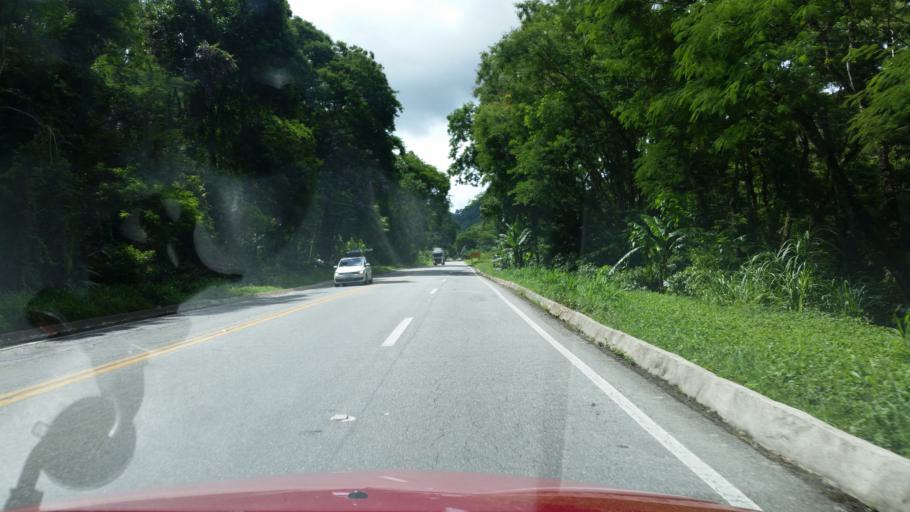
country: BR
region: Sao Paulo
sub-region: Miracatu
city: Miracatu
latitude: -24.3355
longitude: -47.5023
